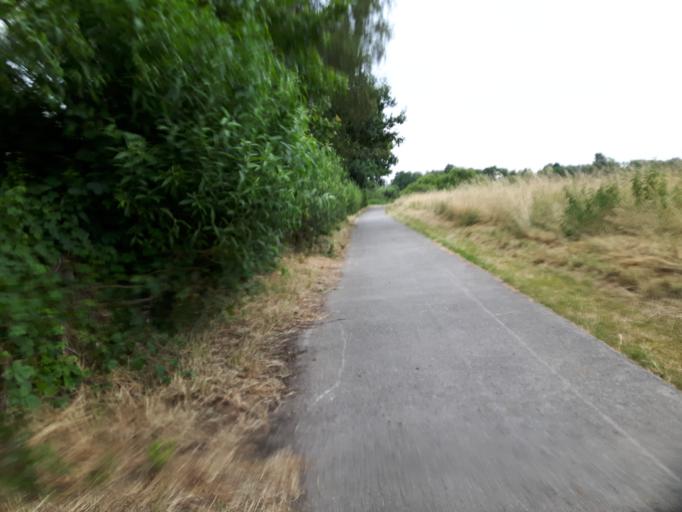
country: DE
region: Lower Saxony
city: Stelle
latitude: 53.4083
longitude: 10.0740
